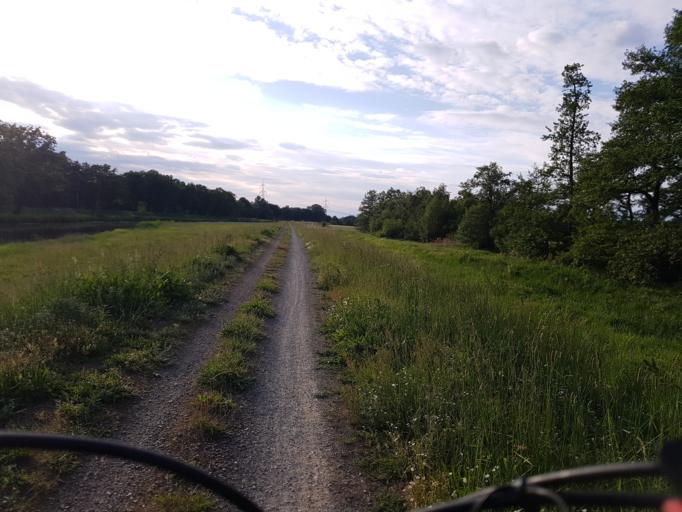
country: DE
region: Brandenburg
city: Bad Liebenwerda
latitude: 51.4917
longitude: 13.4269
